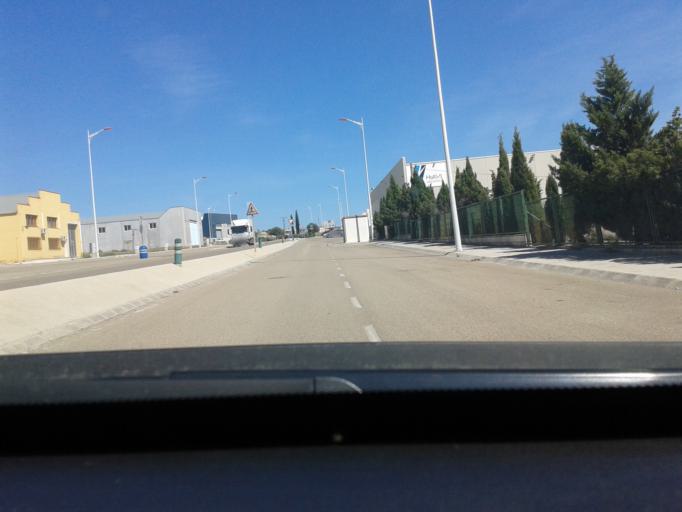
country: ES
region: Castille-La Mancha
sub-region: Provincia de Albacete
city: Caudete
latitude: 38.7128
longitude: -0.9690
